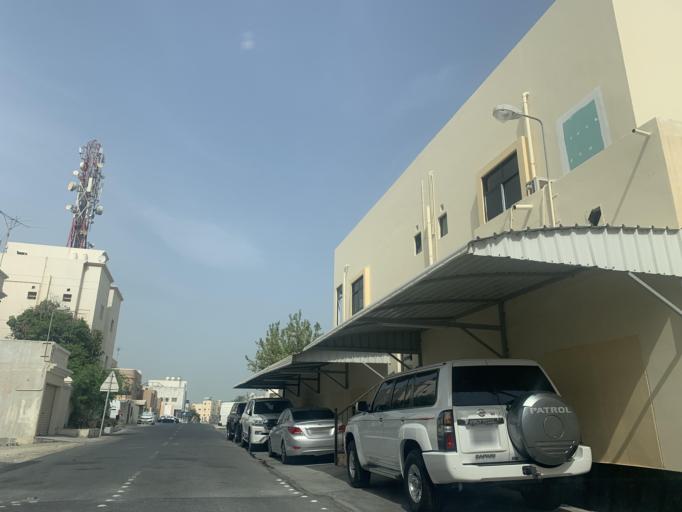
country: BH
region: Northern
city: Ar Rifa'
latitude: 26.1310
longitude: 50.5518
